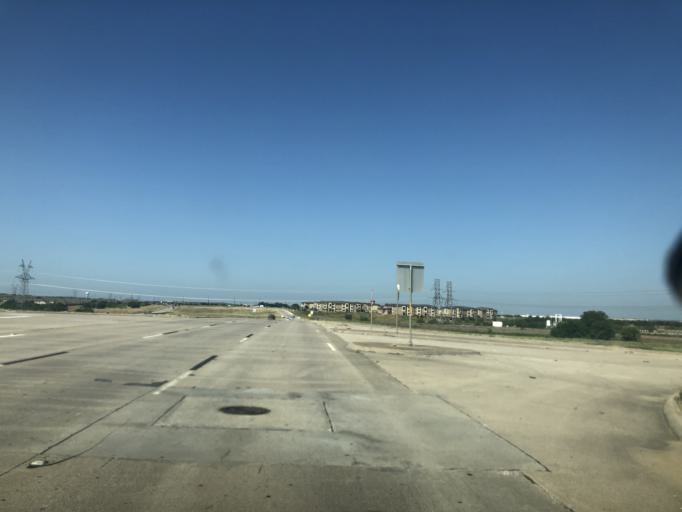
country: US
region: Texas
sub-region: Tarrant County
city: Keller
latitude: 32.9693
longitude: -97.2881
